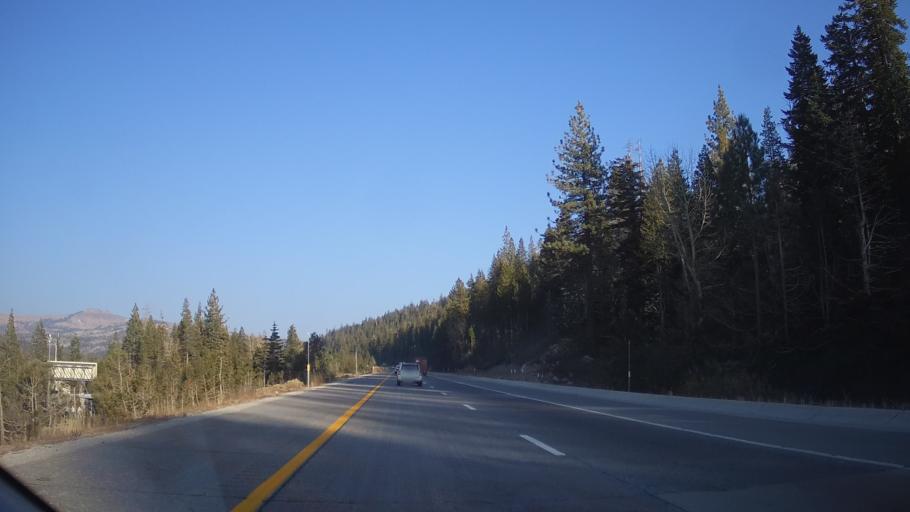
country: US
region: California
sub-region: Nevada County
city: Truckee
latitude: 39.3152
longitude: -120.4404
